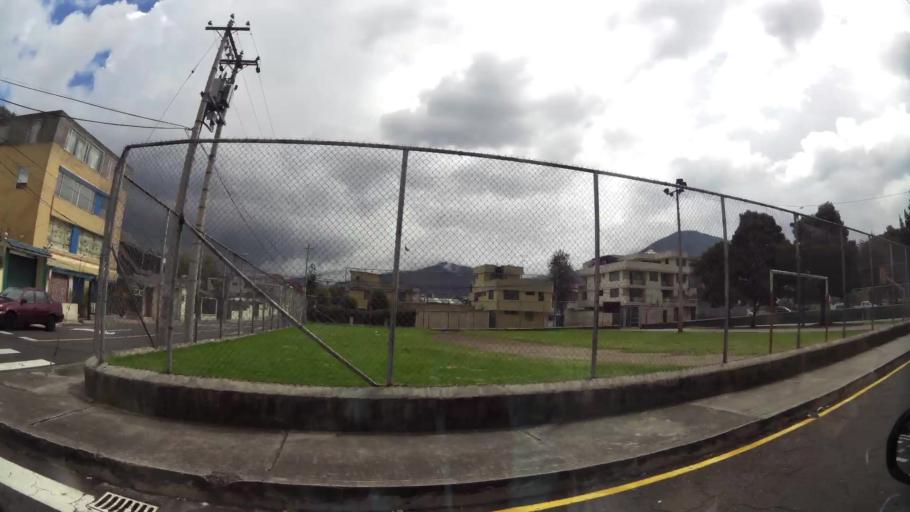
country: EC
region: Pichincha
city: Quito
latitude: -0.2520
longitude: -78.5266
